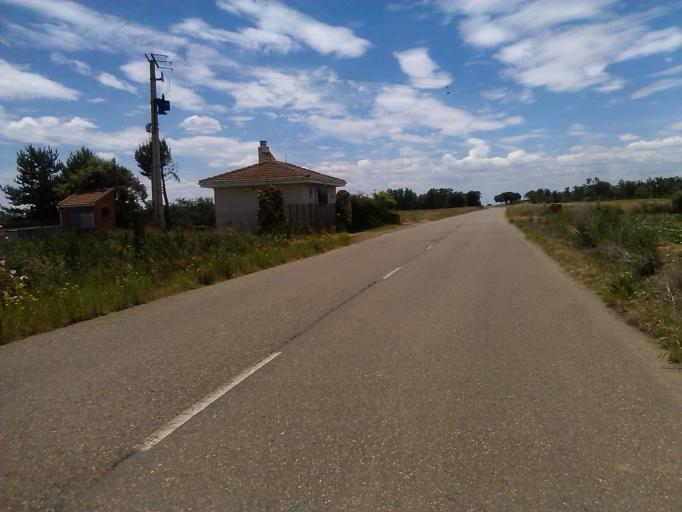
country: ES
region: Castille and Leon
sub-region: Provincia de Leon
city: Chozas de Abajo
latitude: 42.4979
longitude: -5.7054
